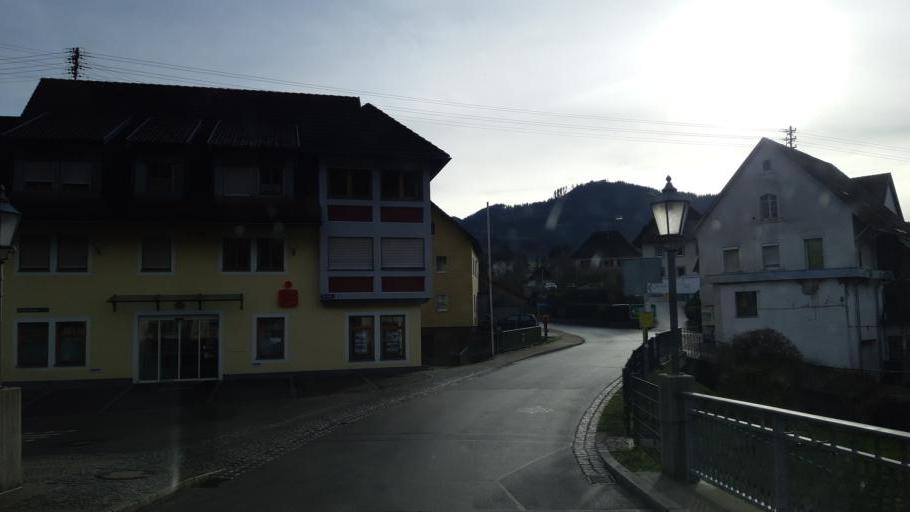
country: DE
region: Baden-Wuerttemberg
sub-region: Freiburg Region
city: Elzach
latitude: 48.1537
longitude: 8.0434
